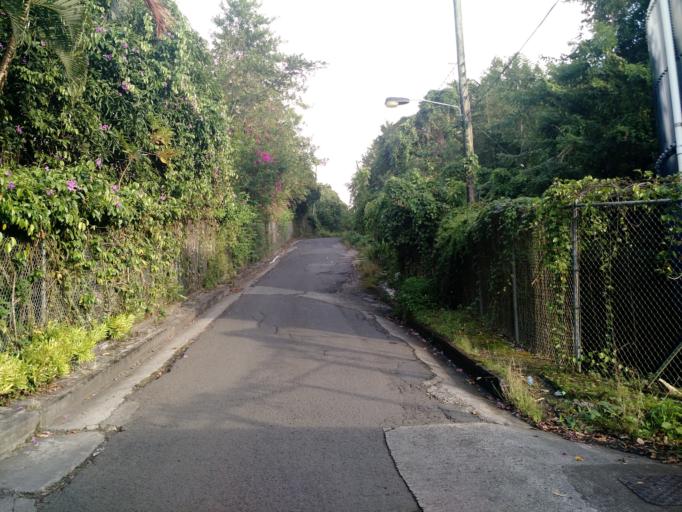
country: LC
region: Anse-la-Raye
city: Anse La Raye
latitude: 13.9636
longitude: -61.0231
